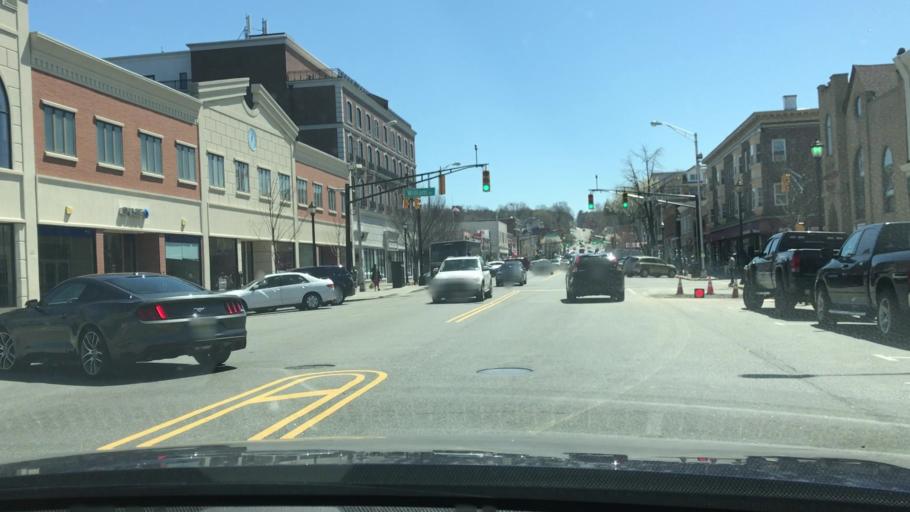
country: US
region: New Jersey
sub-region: Bergen County
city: Englewood
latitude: 40.8957
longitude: -73.9779
